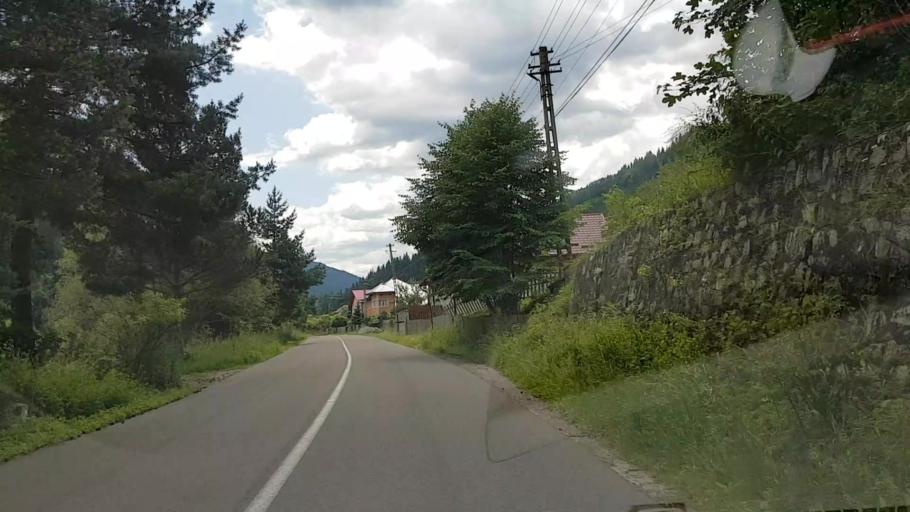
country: RO
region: Suceava
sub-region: Comuna Crucea
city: Crucea
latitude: 47.3454
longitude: 25.6078
